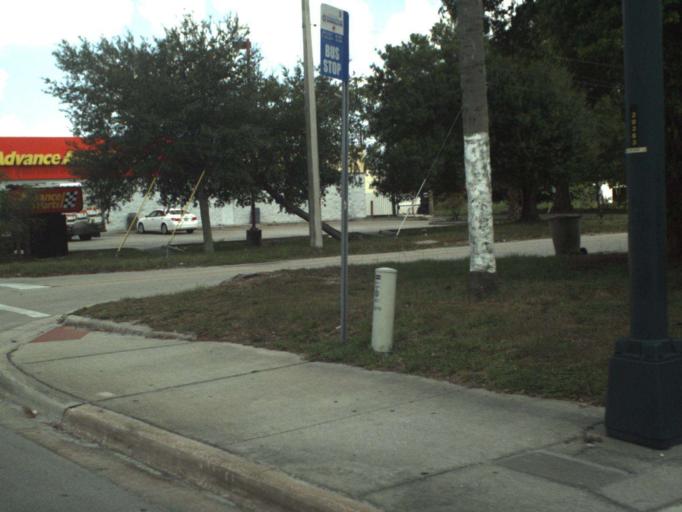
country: US
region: Florida
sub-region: Saint Lucie County
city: Fort Pierce
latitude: 27.4475
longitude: -80.3487
